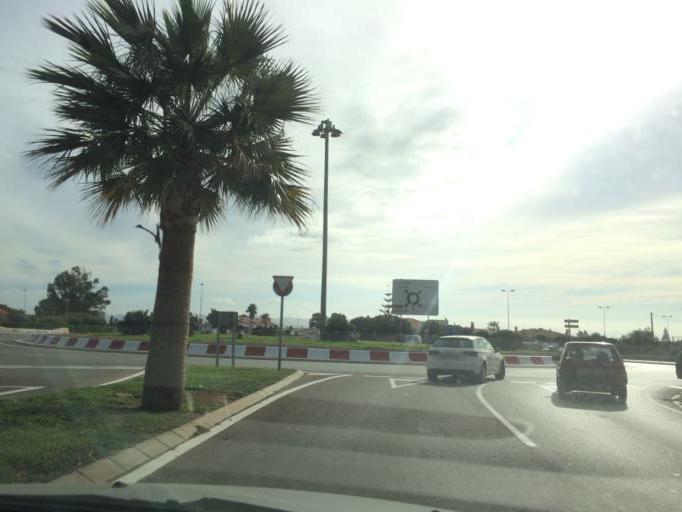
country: ES
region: Andalusia
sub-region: Provincia de Almeria
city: Retamar
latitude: 36.8445
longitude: -2.3047
